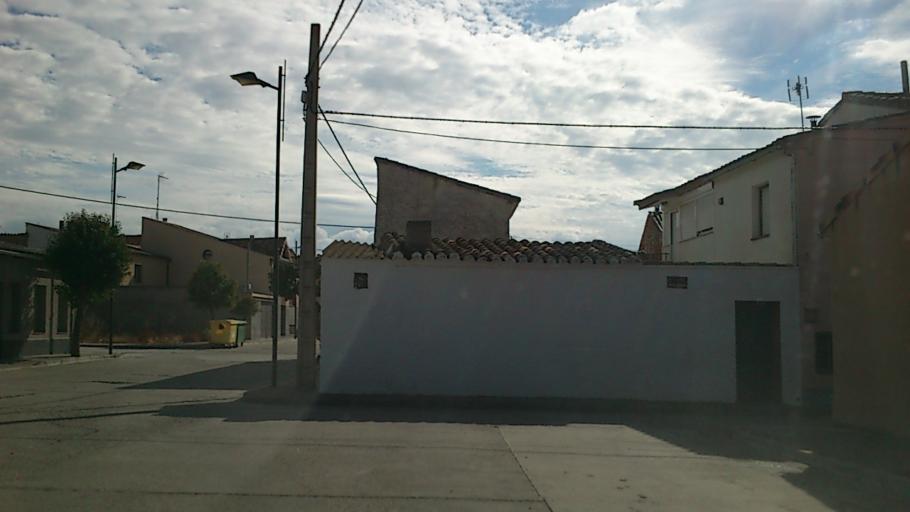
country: ES
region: Aragon
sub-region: Provincia de Zaragoza
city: San Mateo de Gallego
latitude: 41.8292
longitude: -0.7658
